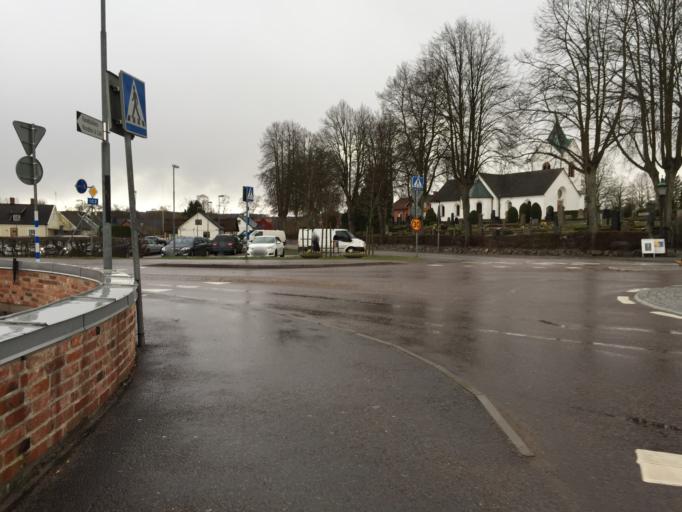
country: SE
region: Skane
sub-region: Lunds Kommun
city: Veberod
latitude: 55.6352
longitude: 13.4908
